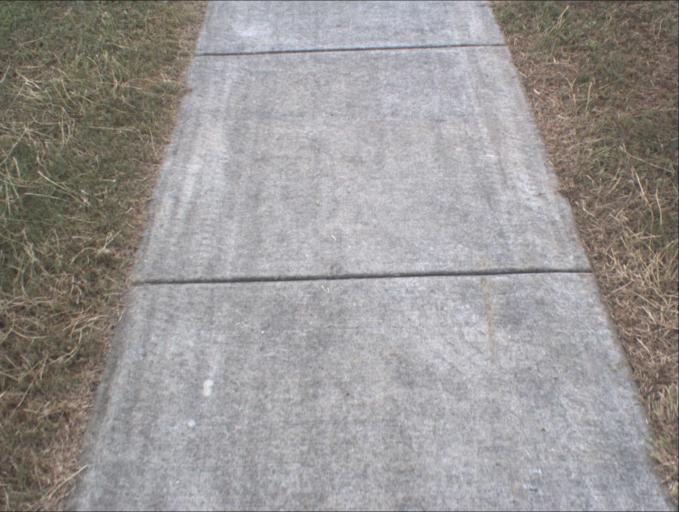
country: AU
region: Queensland
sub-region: Logan
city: Slacks Creek
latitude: -27.6624
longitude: 153.1317
